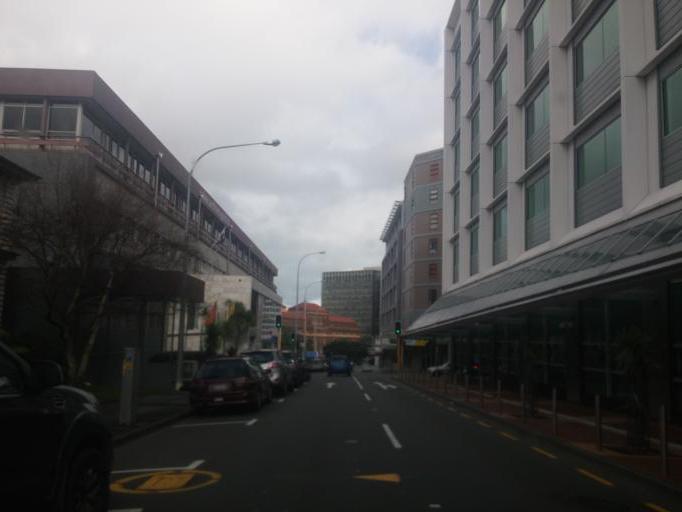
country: NZ
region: Wellington
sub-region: Wellington City
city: Wellington
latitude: -41.2764
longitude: 174.7799
